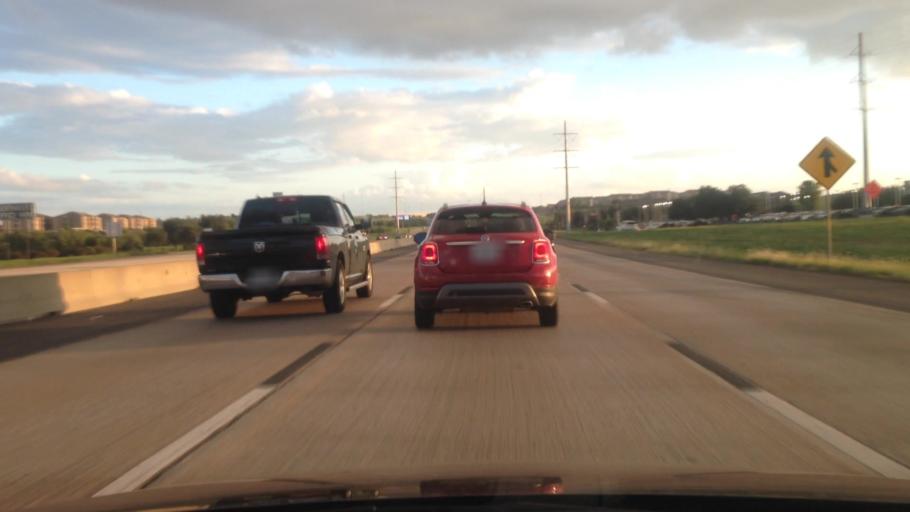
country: US
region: Texas
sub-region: Tarrant County
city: White Settlement
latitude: 32.7578
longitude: -97.4785
